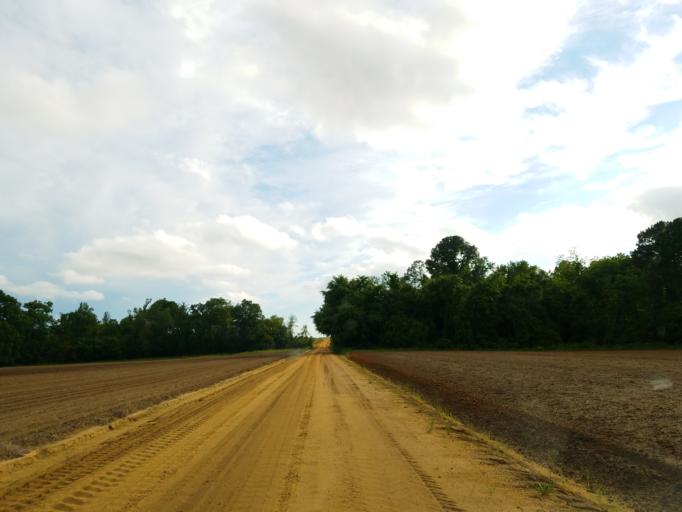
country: US
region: Georgia
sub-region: Dooly County
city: Vienna
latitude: 32.1513
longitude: -83.7767
